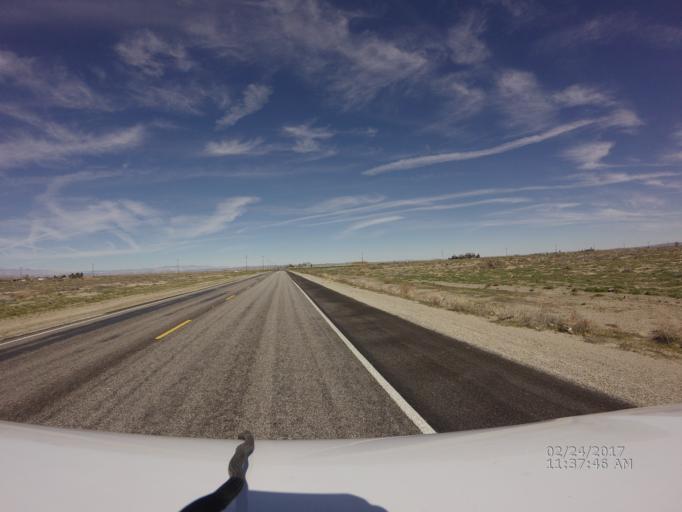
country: US
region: California
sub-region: Los Angeles County
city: Lancaster
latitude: 34.6955
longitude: -118.0412
